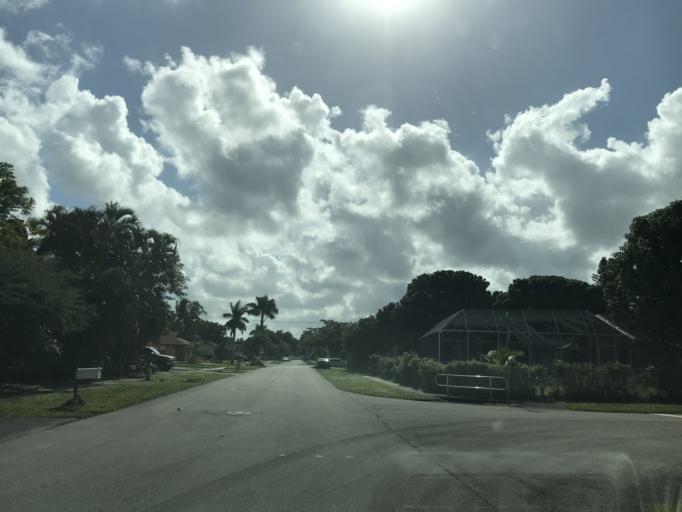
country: US
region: Florida
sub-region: Broward County
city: Coconut Creek
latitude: 26.2646
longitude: -80.1930
